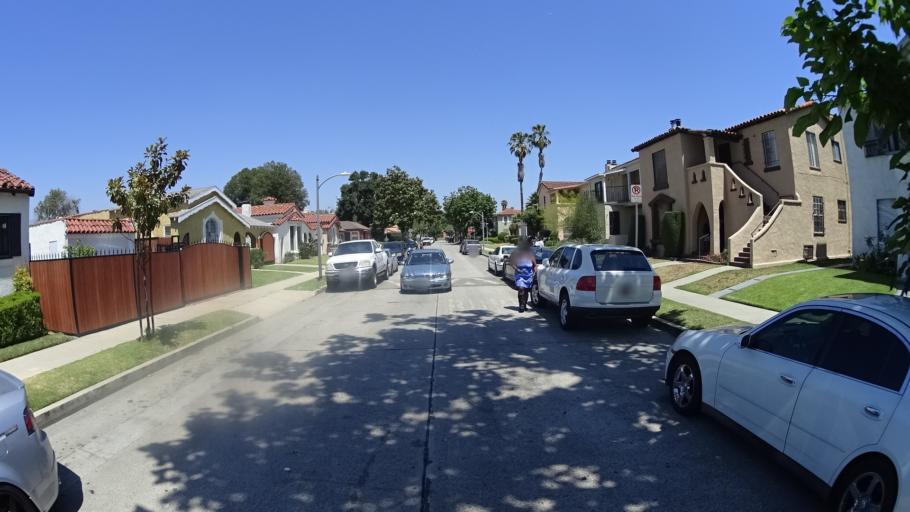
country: US
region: California
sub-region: Los Angeles County
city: View Park-Windsor Hills
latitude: 34.0044
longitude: -118.3245
